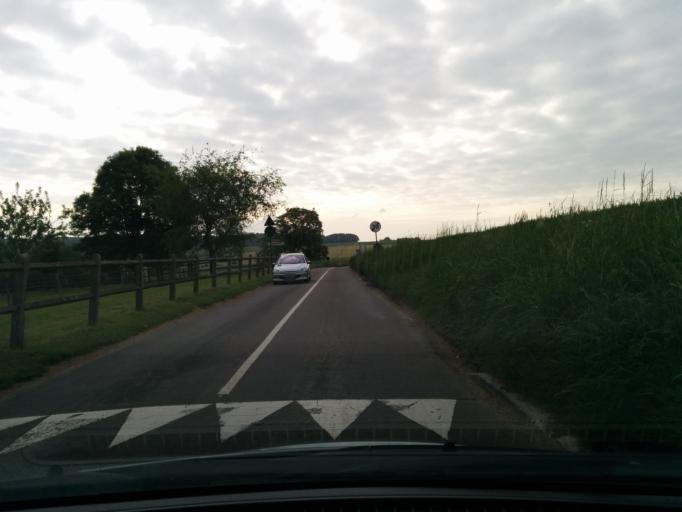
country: FR
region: Haute-Normandie
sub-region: Departement de l'Eure
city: Gasny
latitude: 49.0868
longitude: 1.6763
